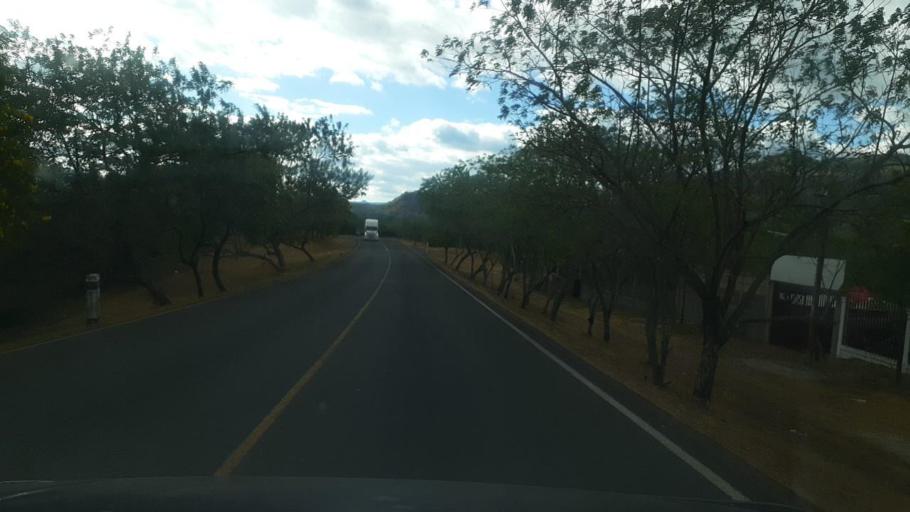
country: NI
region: Madriz
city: Somoto
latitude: 13.4721
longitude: -86.6129
